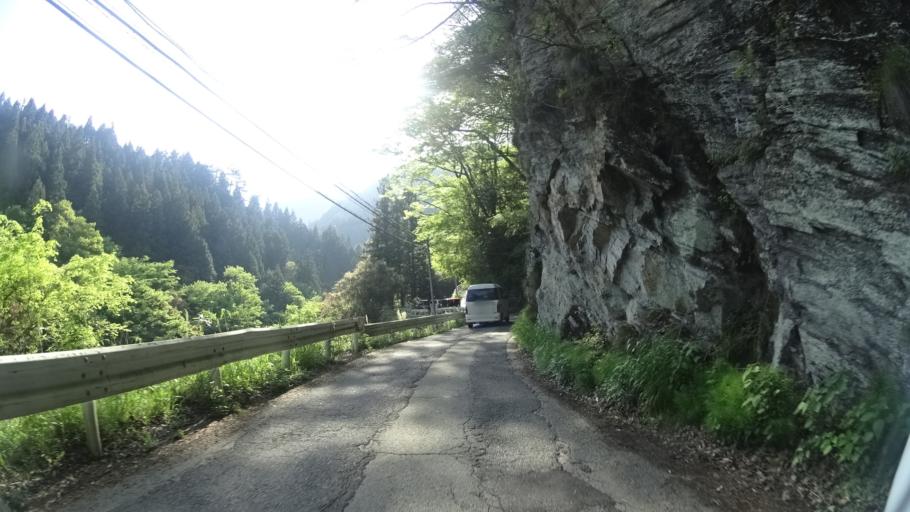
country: JP
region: Tokushima
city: Ikedacho
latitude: 33.8819
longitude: 133.9311
